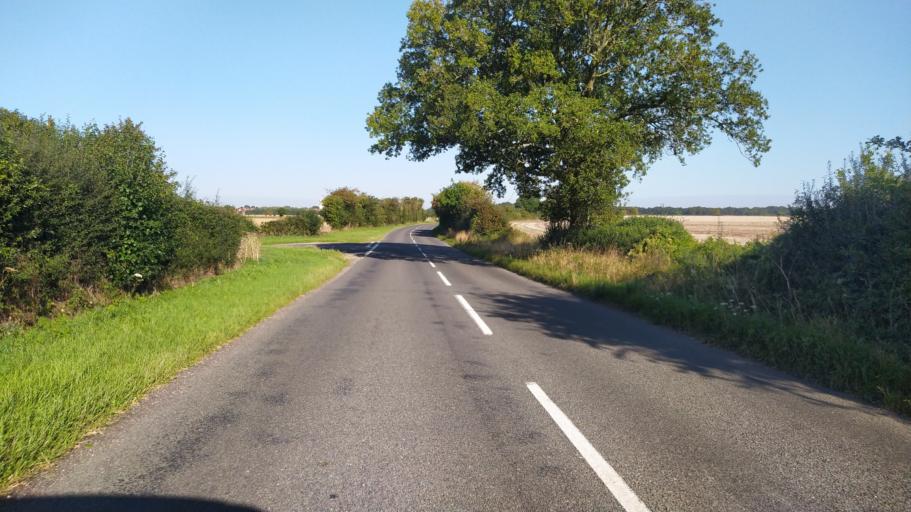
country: GB
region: England
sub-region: Hampshire
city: Abbotts Ann
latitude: 51.1498
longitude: -1.5446
